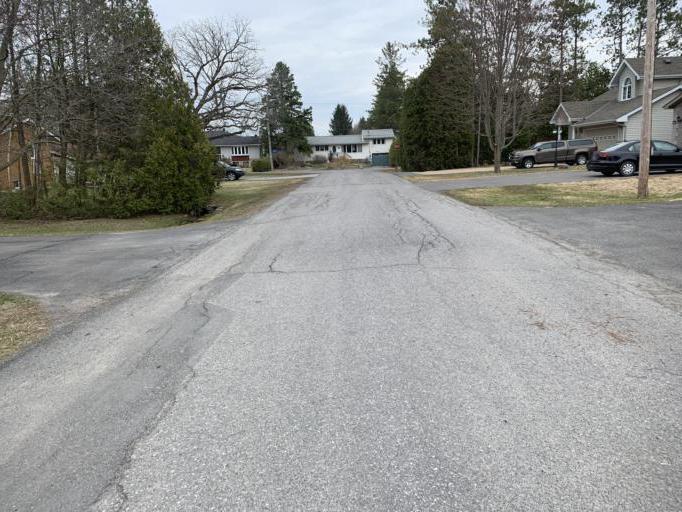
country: CA
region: Ontario
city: Bells Corners
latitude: 45.1838
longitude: -75.8307
